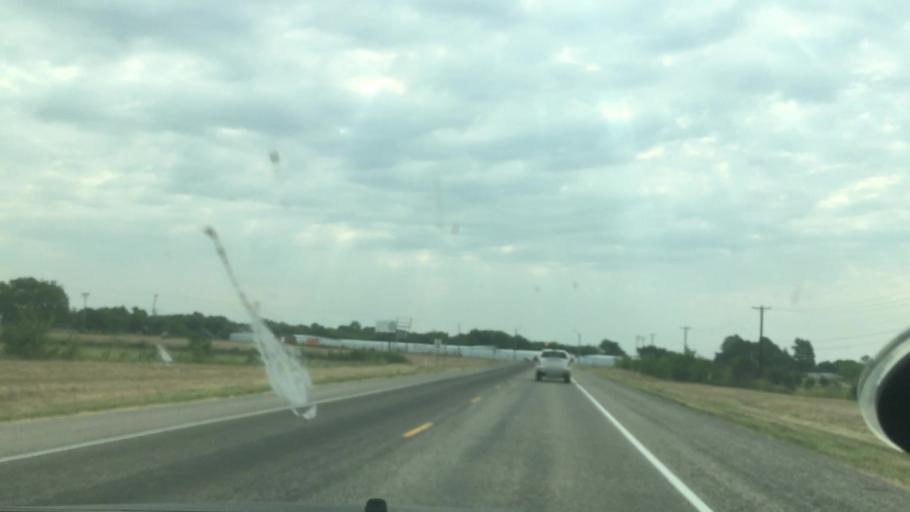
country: US
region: Texas
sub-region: Grayson County
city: Pottsboro
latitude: 33.7964
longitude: -96.6153
